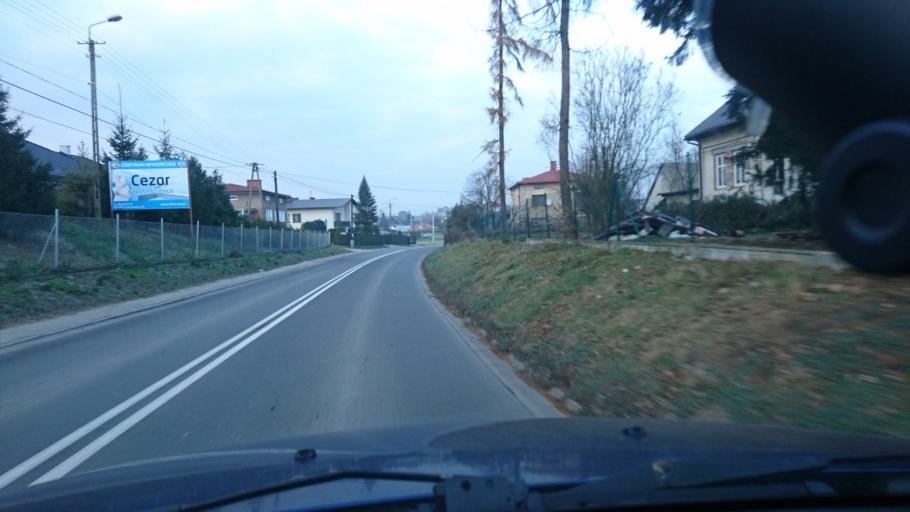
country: PL
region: Silesian Voivodeship
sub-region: Powiat bielski
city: Bestwina
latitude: 49.9039
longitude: 19.0543
